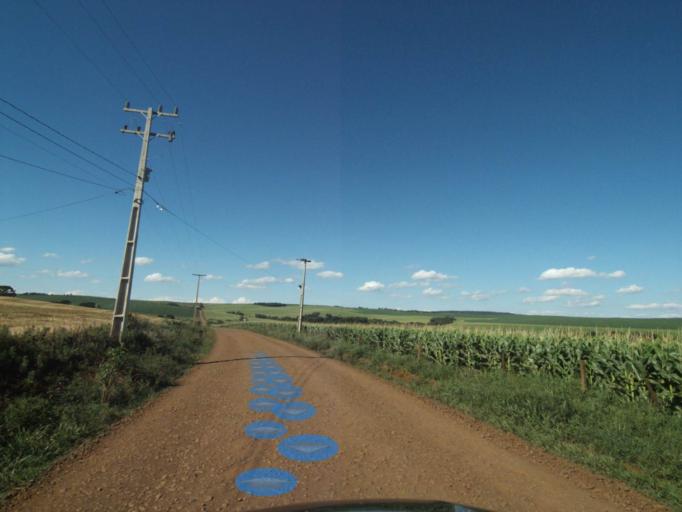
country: BR
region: Parana
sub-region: Coronel Vivida
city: Coronel Vivida
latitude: -26.1360
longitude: -52.3929
